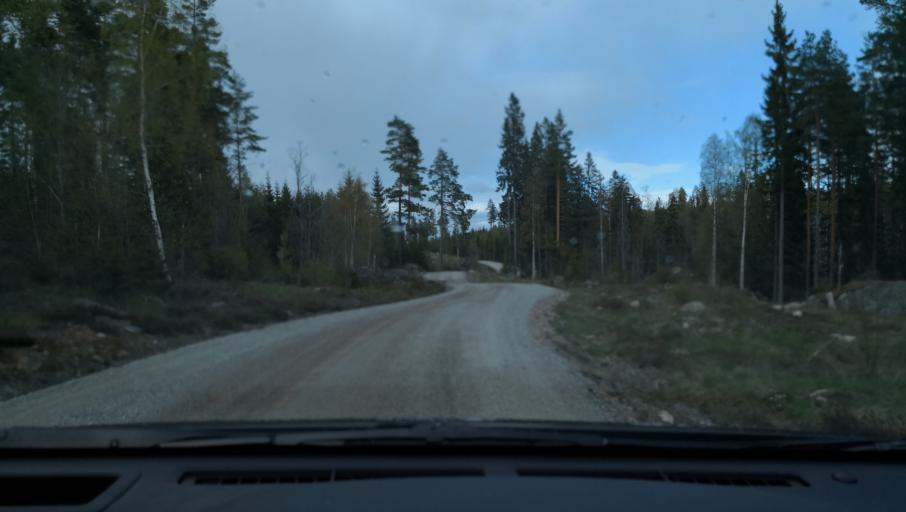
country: SE
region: Dalarna
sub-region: Saters Kommun
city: Saeter
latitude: 60.1882
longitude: 15.7345
